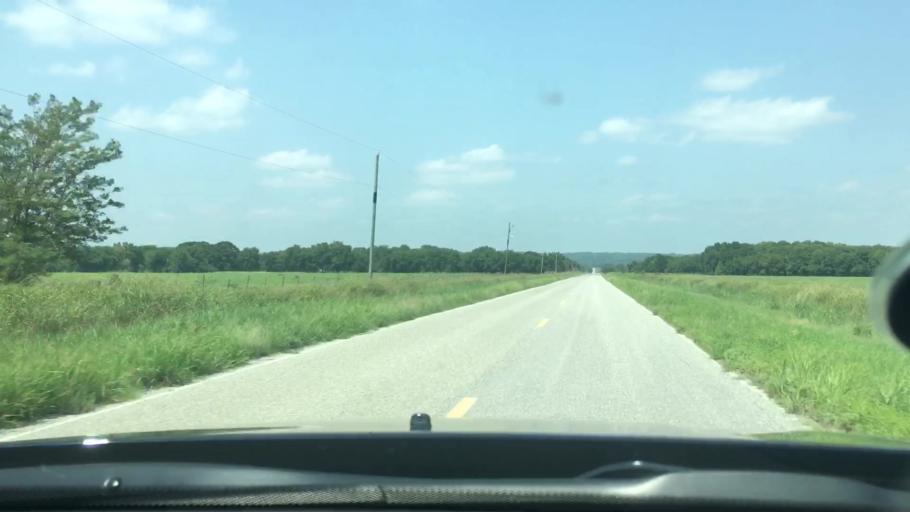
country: US
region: Oklahoma
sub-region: Johnston County
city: Tishomingo
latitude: 34.3811
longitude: -96.4962
